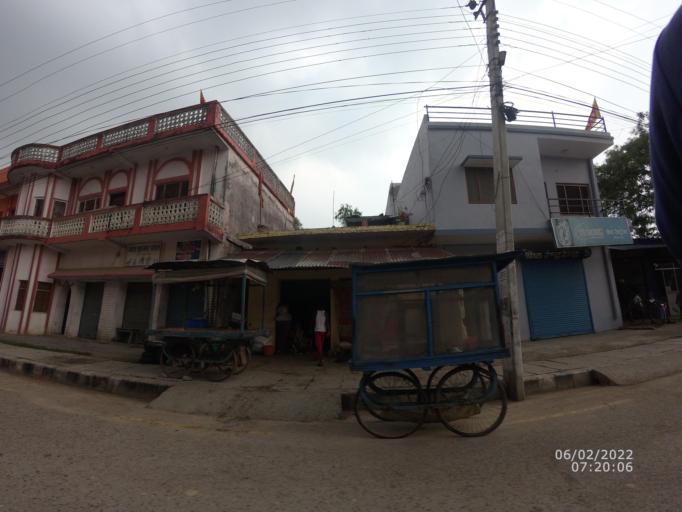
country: NP
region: Western Region
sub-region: Lumbini Zone
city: Bhairahawa
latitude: 27.4844
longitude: 83.4410
